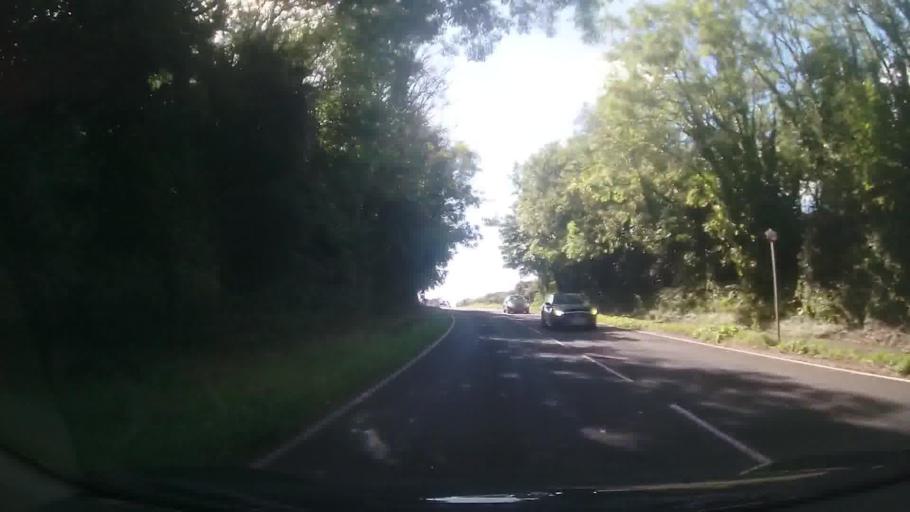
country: GB
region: Wales
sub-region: Pembrokeshire
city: Penally
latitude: 51.6678
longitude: -4.7239
